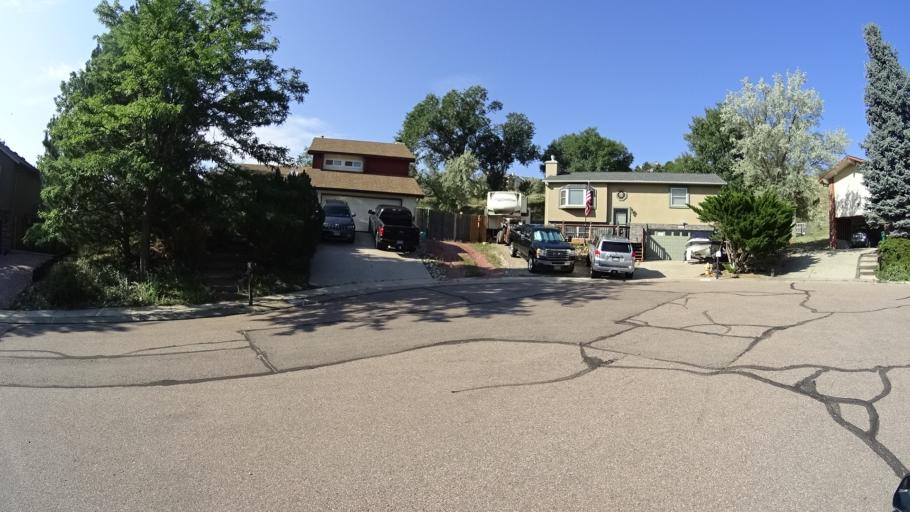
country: US
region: Colorado
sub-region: El Paso County
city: Colorado Springs
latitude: 38.8844
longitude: -104.8439
